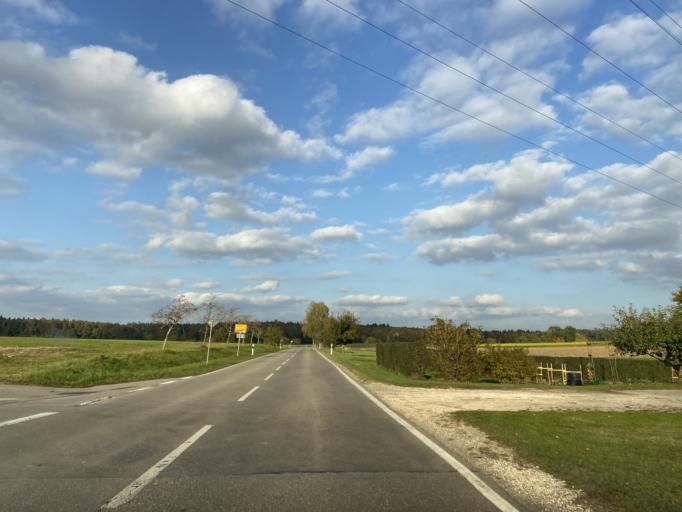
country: DE
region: Baden-Wuerttemberg
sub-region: Tuebingen Region
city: Scheer
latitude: 48.0956
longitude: 9.3320
